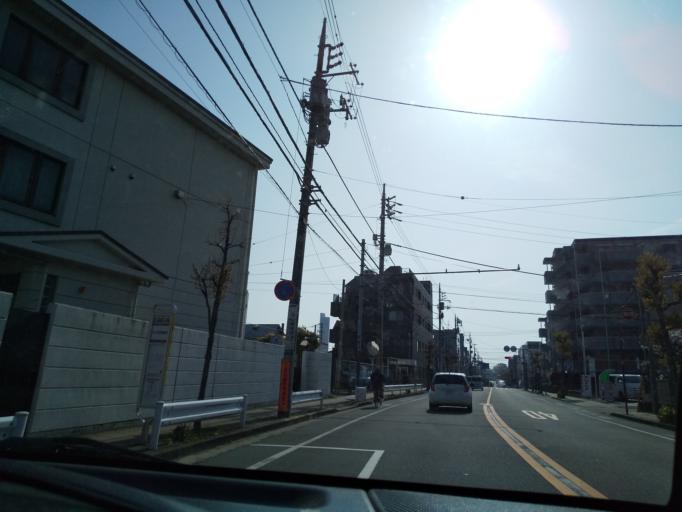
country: JP
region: Tokyo
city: Hino
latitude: 35.6982
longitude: 139.4005
